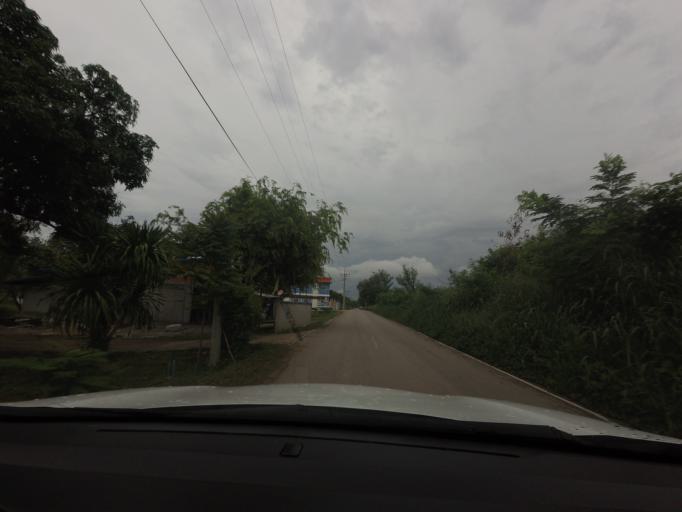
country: TH
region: Nakhon Ratchasima
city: Pak Chong
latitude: 14.6553
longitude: 101.4194
